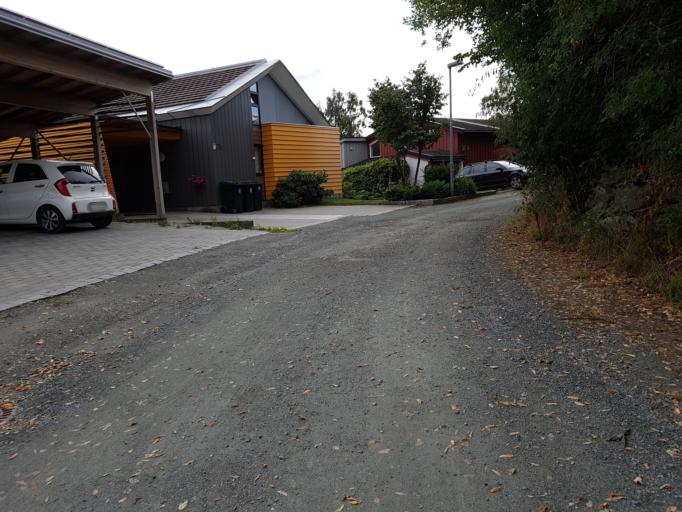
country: NO
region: Sor-Trondelag
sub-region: Trondheim
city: Trondheim
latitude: 63.4447
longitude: 10.4274
